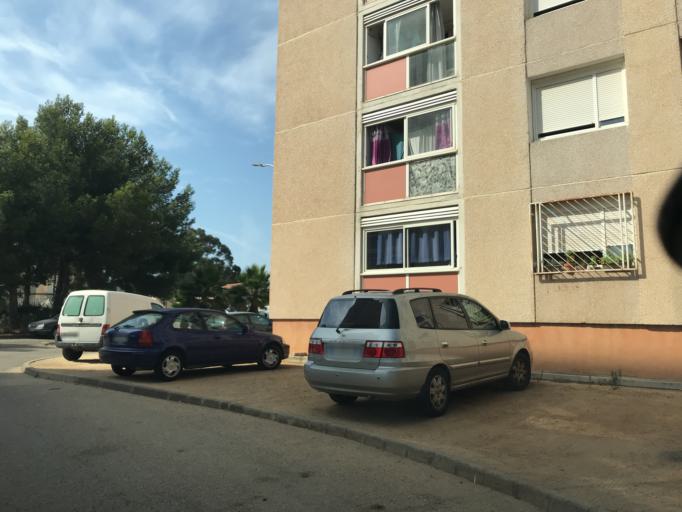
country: FR
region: Provence-Alpes-Cote d'Azur
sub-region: Departement du Var
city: La Seyne-sur-Mer
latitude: 43.0860
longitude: 5.8828
